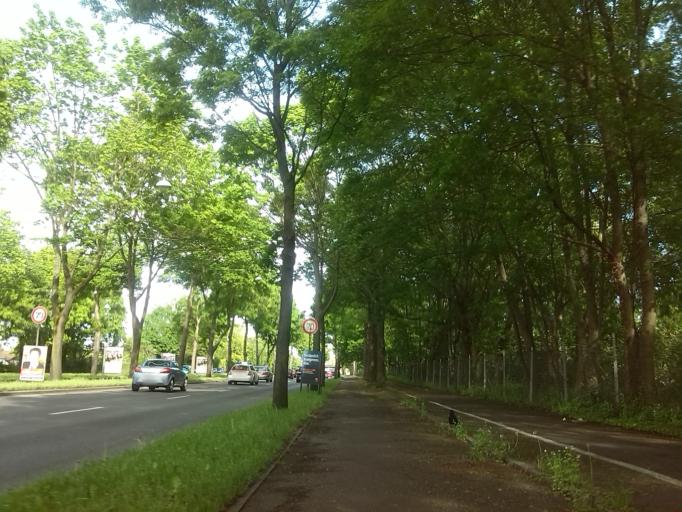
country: DE
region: Baden-Wuerttemberg
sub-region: Karlsruhe Region
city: Mannheim
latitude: 49.4892
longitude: 8.5042
